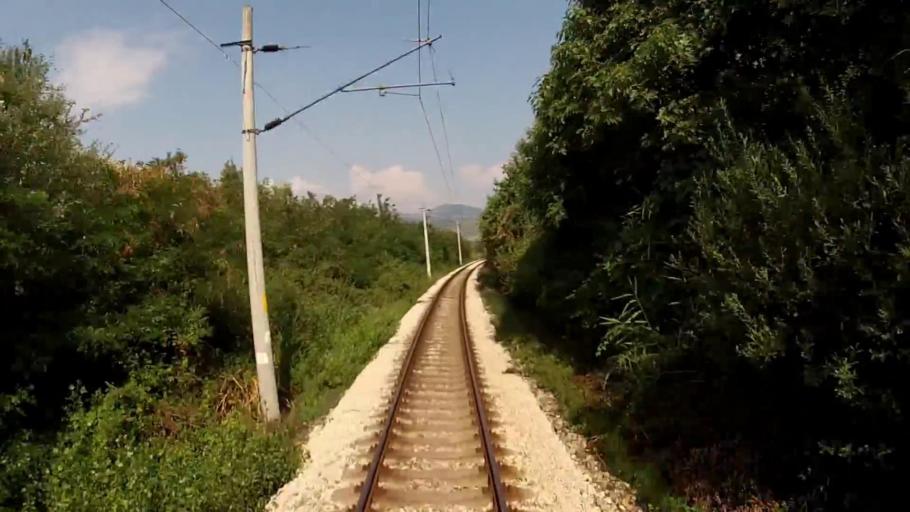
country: BG
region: Blagoevgrad
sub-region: Obshtina Sandanski
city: Sandanski
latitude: 41.5294
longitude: 23.2606
